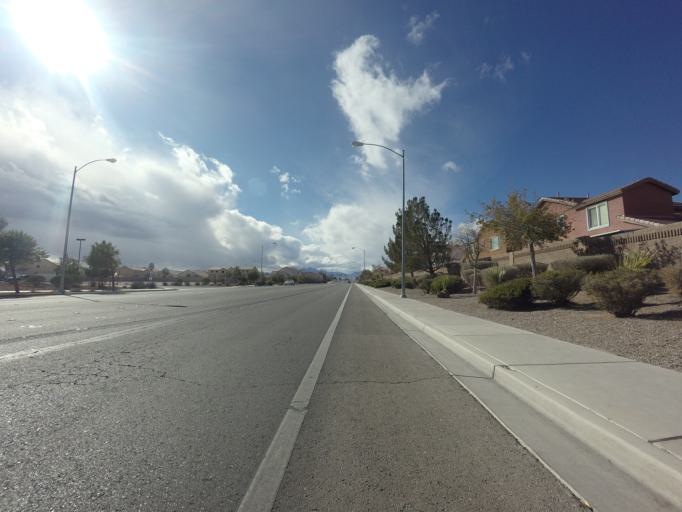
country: US
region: Nevada
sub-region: Clark County
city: North Las Vegas
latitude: 36.2543
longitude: -115.1310
